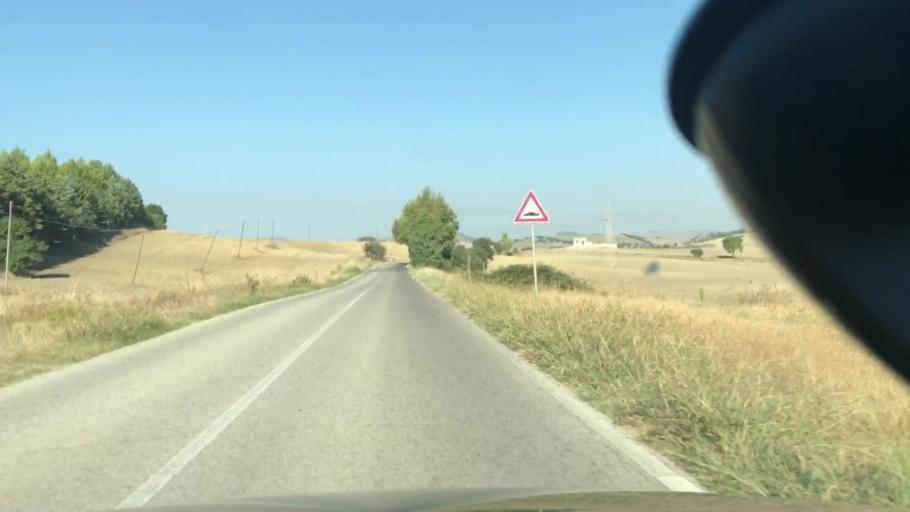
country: IT
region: Basilicate
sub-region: Provincia di Matera
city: La Martella
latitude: 40.6657
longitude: 16.4925
